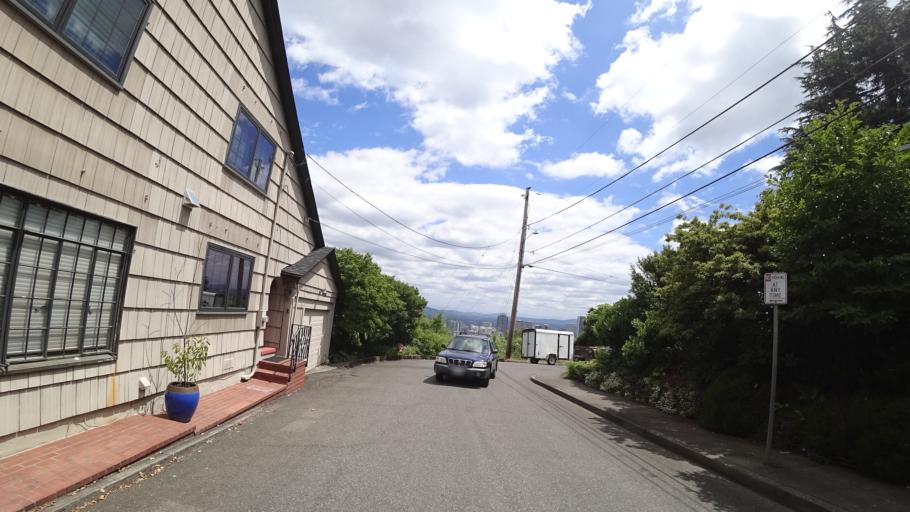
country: US
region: Oregon
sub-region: Multnomah County
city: Portland
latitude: 45.5258
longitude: -122.7028
